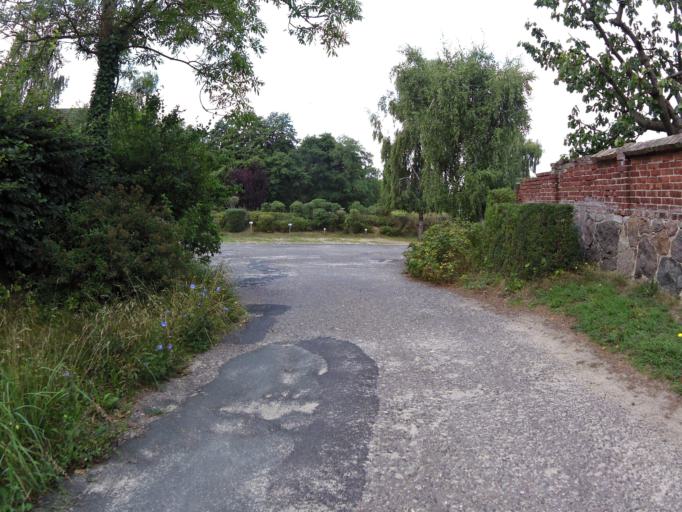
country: DE
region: Mecklenburg-Vorpommern
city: Seebad Bansin
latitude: 53.9589
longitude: 14.0952
